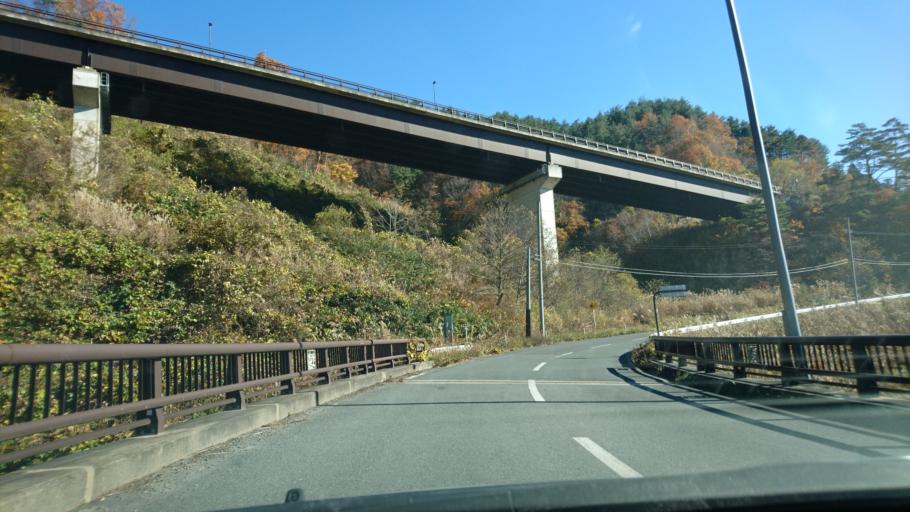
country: JP
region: Iwate
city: Mizusawa
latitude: 39.1236
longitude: 140.9352
